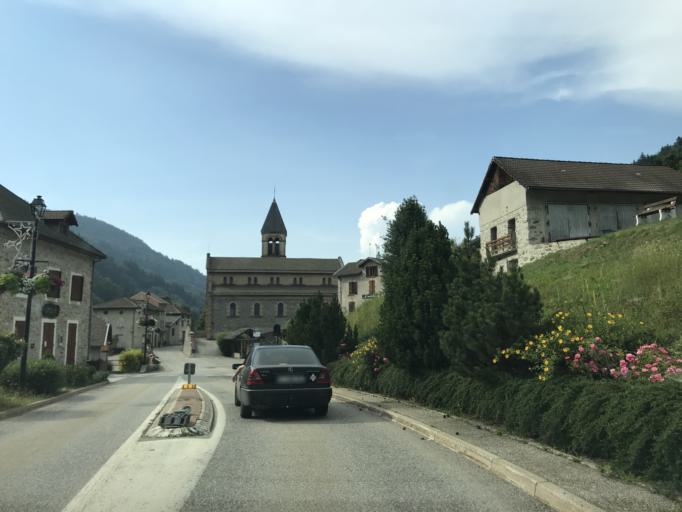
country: FR
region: Rhone-Alpes
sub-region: Departement de l'Isere
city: Allevard
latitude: 45.3565
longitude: 6.1002
